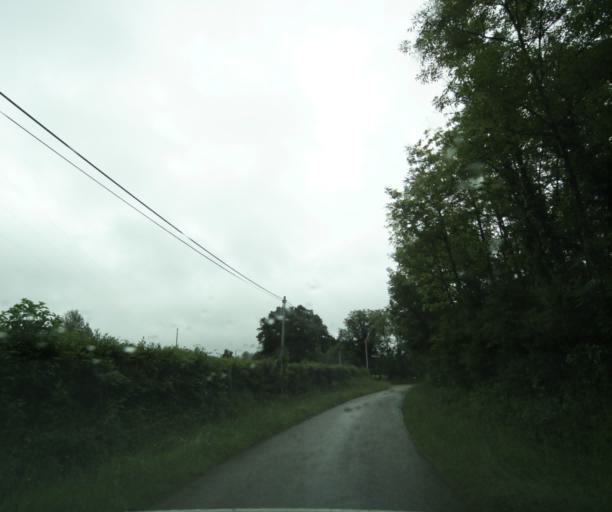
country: FR
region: Bourgogne
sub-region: Departement de Saone-et-Loire
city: Charolles
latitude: 46.5011
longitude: 4.3928
